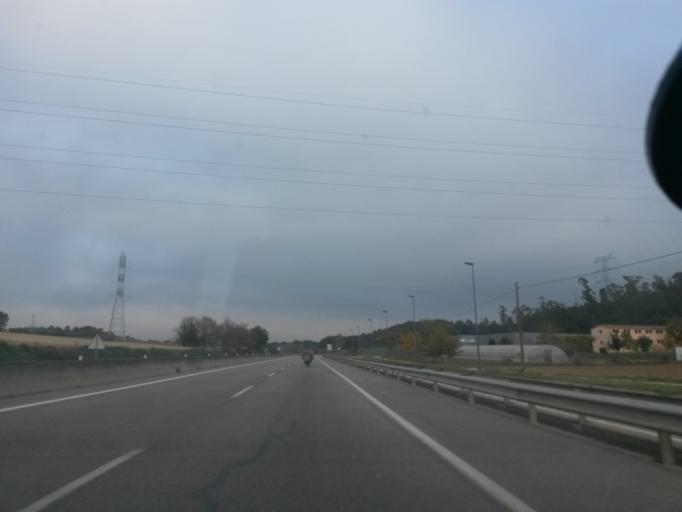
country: ES
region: Catalonia
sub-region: Provincia de Girona
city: Palol de Revardit
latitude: 42.0501
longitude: 2.8186
